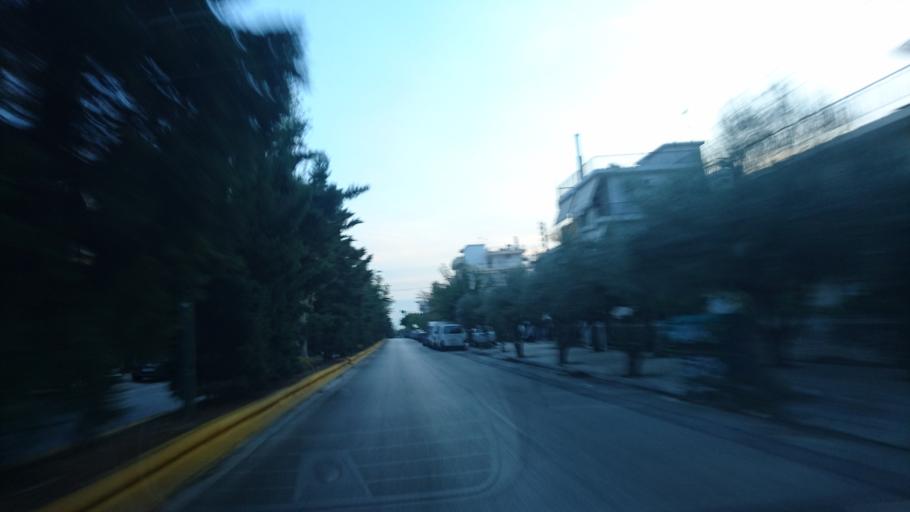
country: GR
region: Attica
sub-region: Nomarchia Athinas
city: Ilioupoli
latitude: 37.9295
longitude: 23.7546
